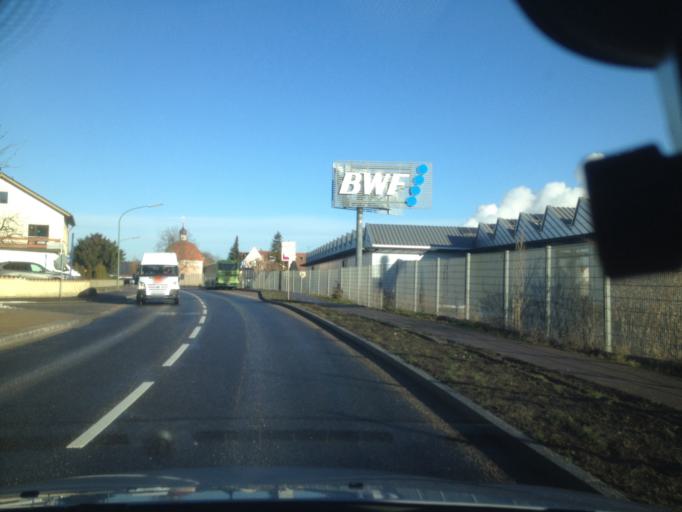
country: DE
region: Bavaria
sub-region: Swabia
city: Offingen
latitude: 48.4773
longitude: 10.3631
